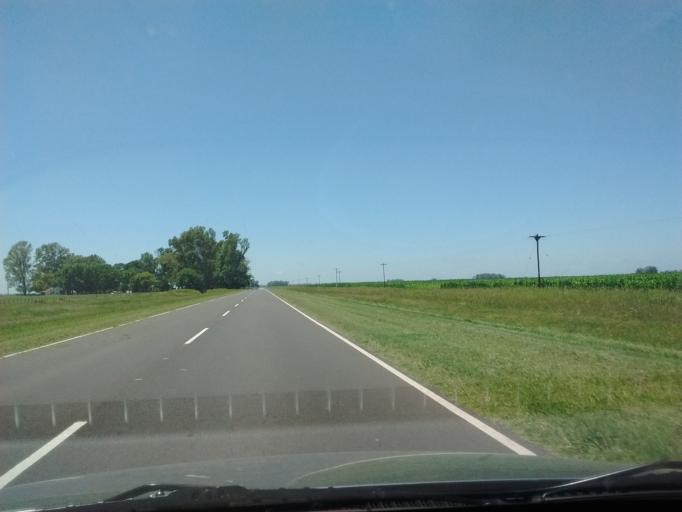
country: AR
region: Entre Rios
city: General Galarza
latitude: -32.9630
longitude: -59.5790
